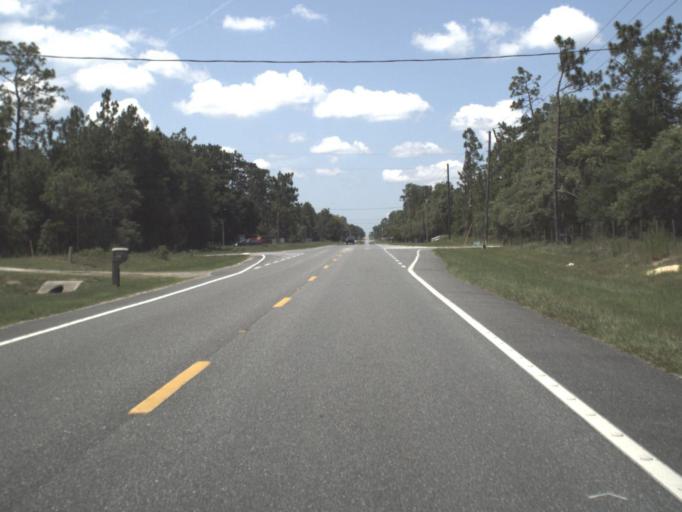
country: US
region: Florida
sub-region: Levy County
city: Williston Highlands
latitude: 29.2964
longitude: -82.5324
